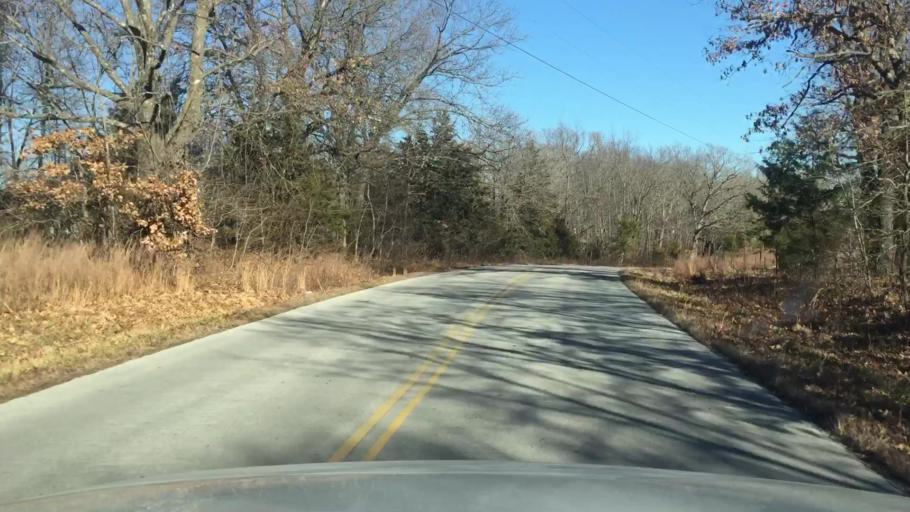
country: US
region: Missouri
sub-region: Morgan County
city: Versailles
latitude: 38.3386
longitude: -92.7582
